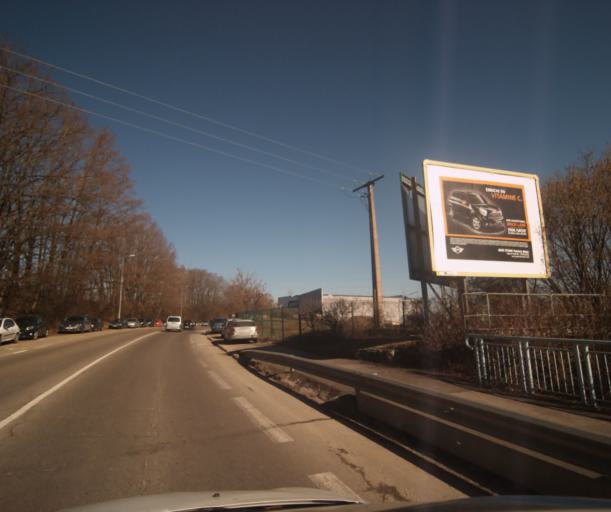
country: FR
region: Franche-Comte
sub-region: Departement du Doubs
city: Avanne-Aveney
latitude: 47.2286
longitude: 5.9658
